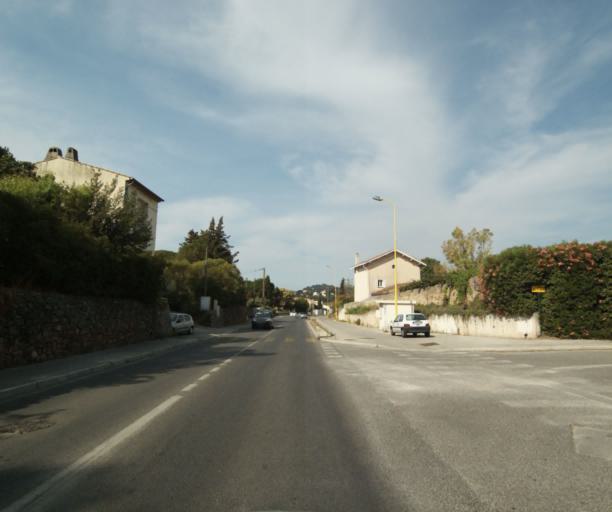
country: FR
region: Provence-Alpes-Cote d'Azur
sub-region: Departement du Var
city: La Garde
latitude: 43.1170
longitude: 5.9894
